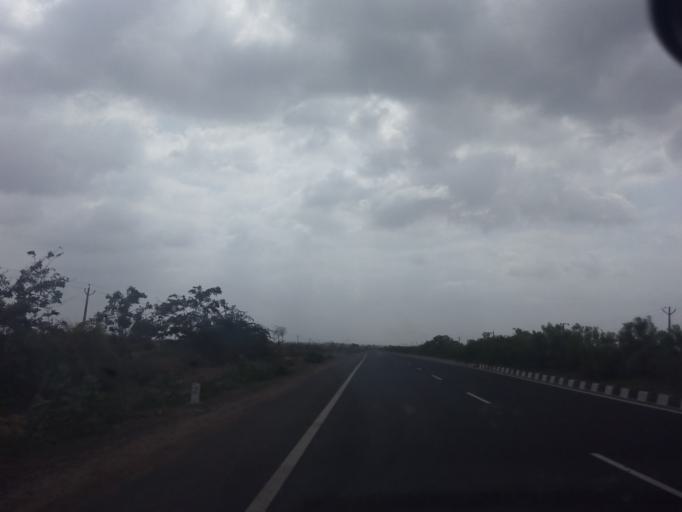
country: IN
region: Gujarat
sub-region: Surendranagar
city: Halvad
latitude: 23.0052
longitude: 71.1204
